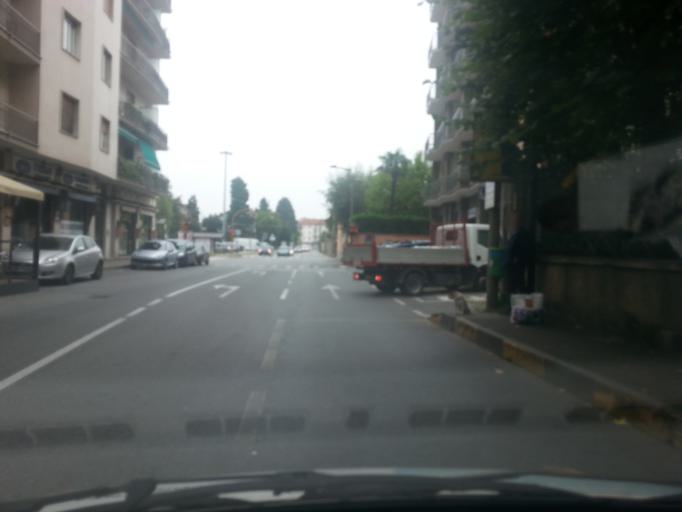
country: IT
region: Piedmont
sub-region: Provincia di Torino
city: Rivoli
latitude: 45.0685
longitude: 7.5207
